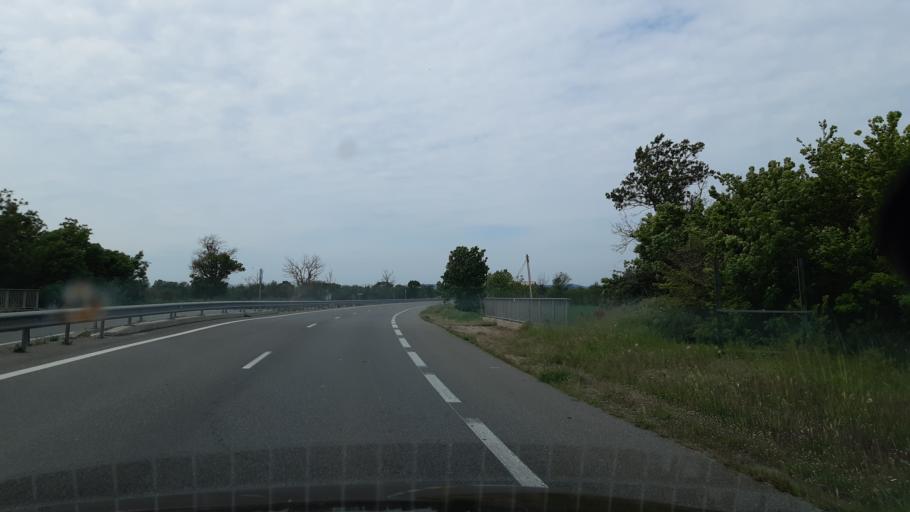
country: FR
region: Languedoc-Roussillon
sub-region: Departement de l'Aude
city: Vinassan
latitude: 43.1730
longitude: 3.0560
